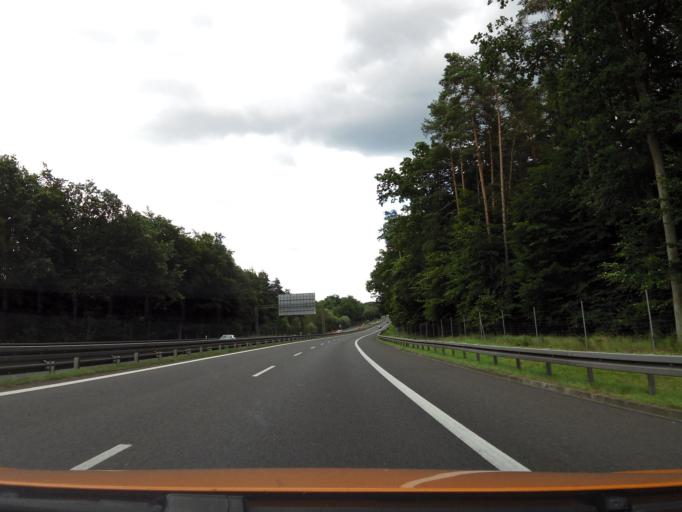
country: PL
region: West Pomeranian Voivodeship
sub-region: Szczecin
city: Szczecin
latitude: 53.3662
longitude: 14.6303
